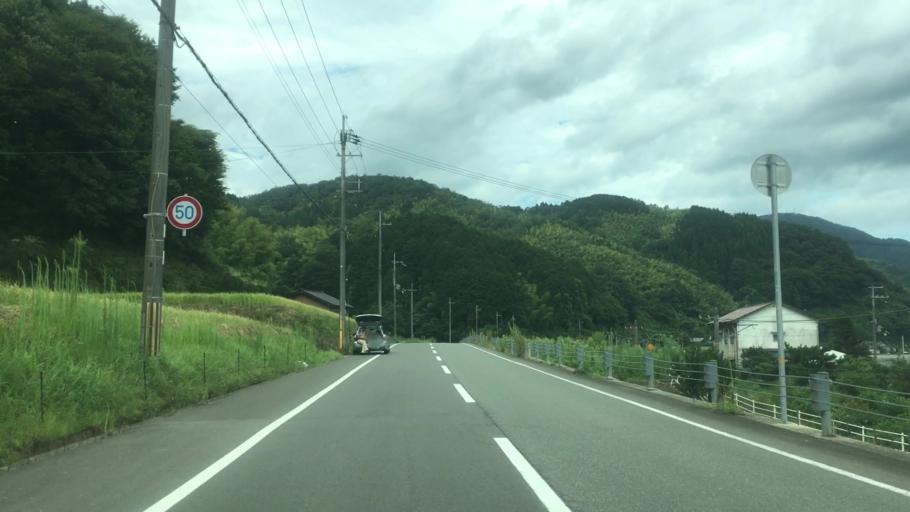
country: JP
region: Hyogo
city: Toyooka
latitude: 35.5772
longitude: 134.8019
